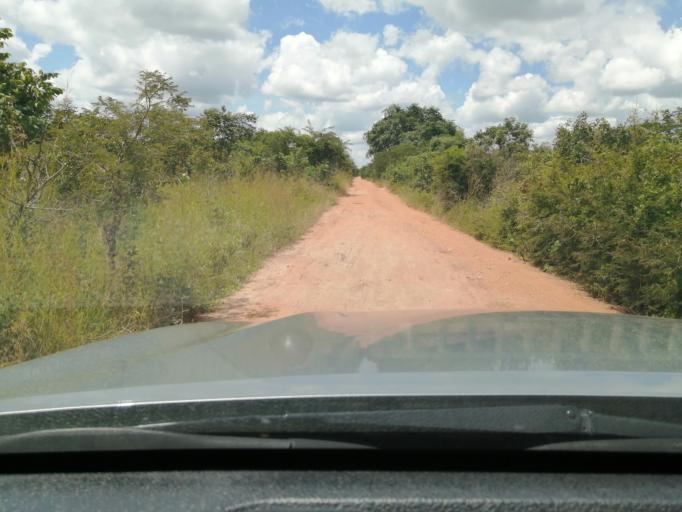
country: ZM
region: Lusaka
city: Lusaka
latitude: -15.1522
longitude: 27.9476
